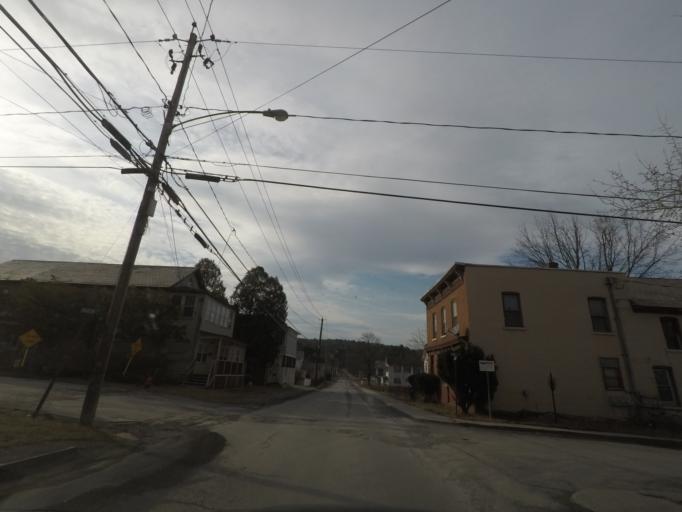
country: US
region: New York
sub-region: Rensselaer County
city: Hoosick Falls
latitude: 42.9073
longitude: -73.3576
